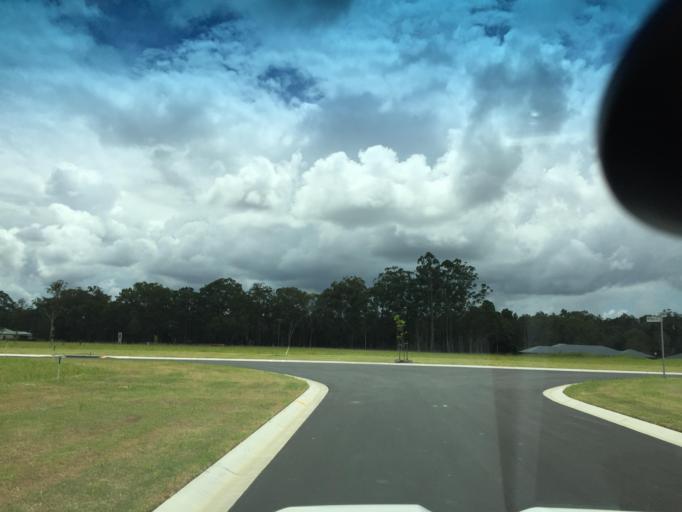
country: AU
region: Queensland
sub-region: Moreton Bay
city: Caboolture
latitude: -27.0420
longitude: 152.9189
